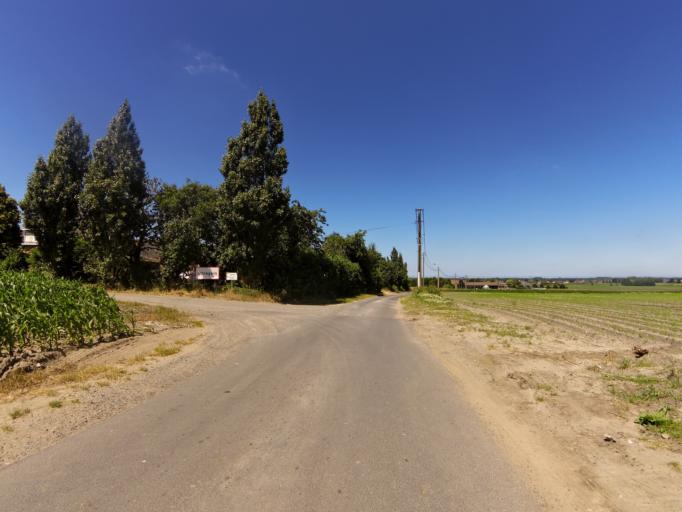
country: BE
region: Flanders
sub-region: Provincie West-Vlaanderen
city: Torhout
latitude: 51.1016
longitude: 3.0669
